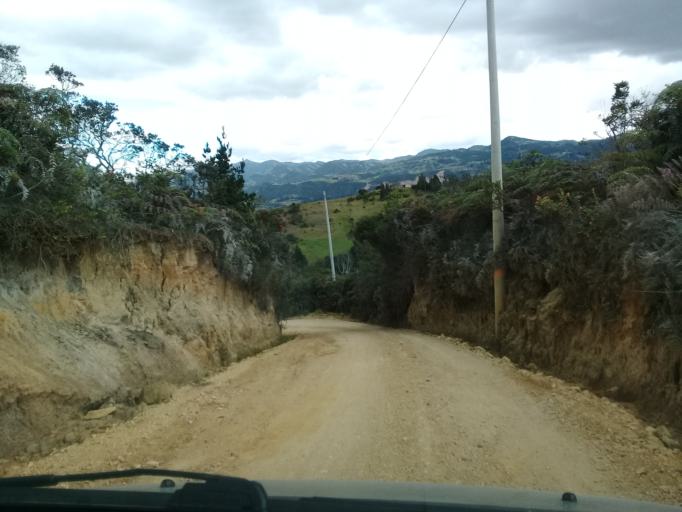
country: CO
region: Cundinamarca
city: Lenguazaque
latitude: 5.2863
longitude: -73.7359
